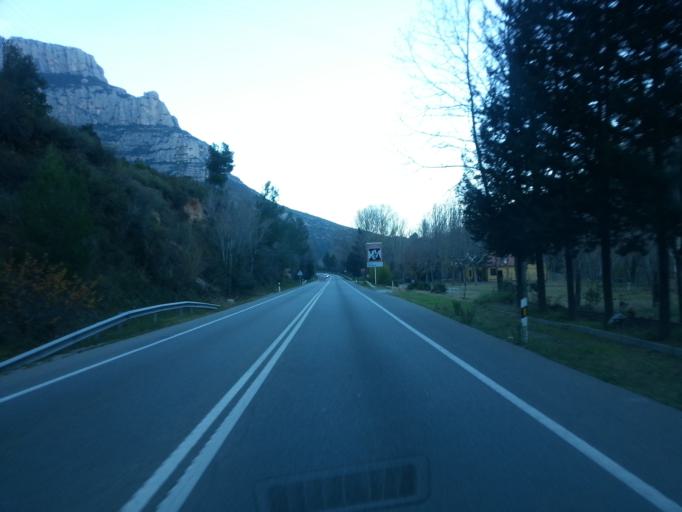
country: ES
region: Catalonia
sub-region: Provincia de Barcelona
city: Collbato
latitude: 41.5850
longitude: 1.8548
